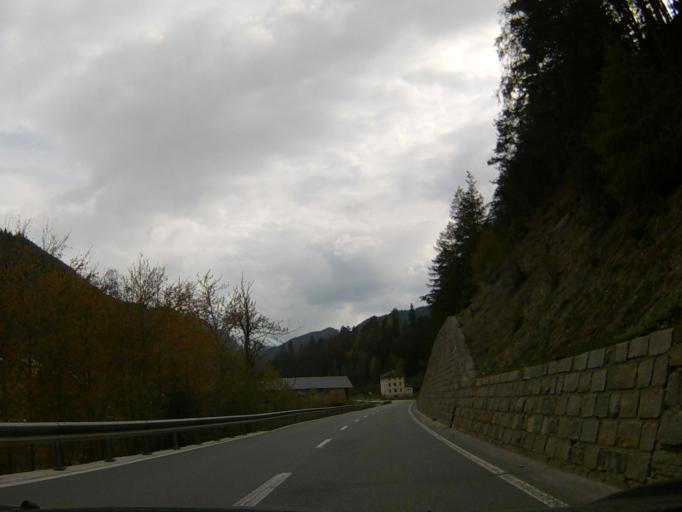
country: AT
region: Tyrol
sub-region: Politischer Bezirk Landeck
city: Nauders
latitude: 46.8728
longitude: 10.4496
